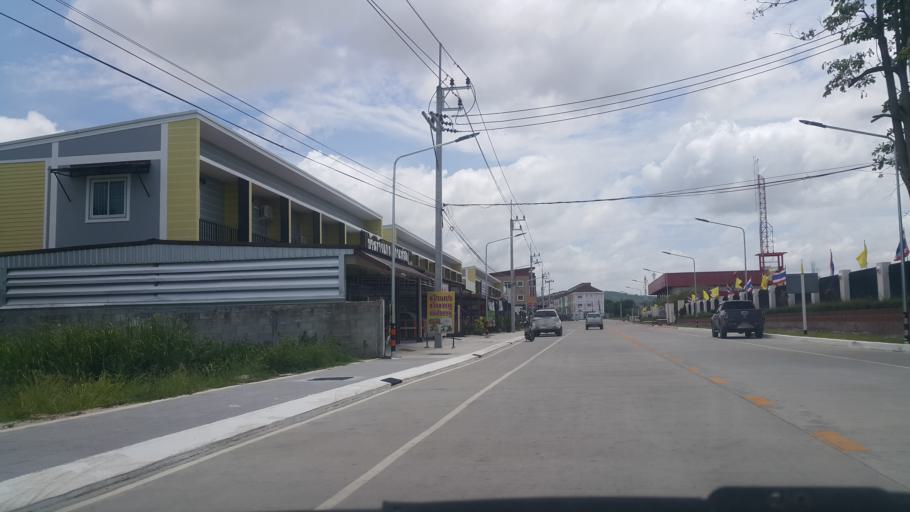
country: TH
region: Rayong
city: Ban Chang
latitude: 12.7202
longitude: 101.0664
